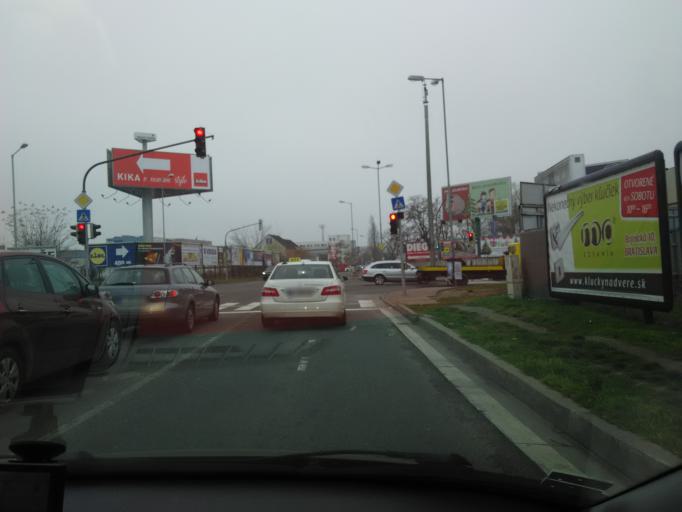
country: SK
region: Bratislavsky
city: Bratislava
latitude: 48.1678
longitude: 17.1779
